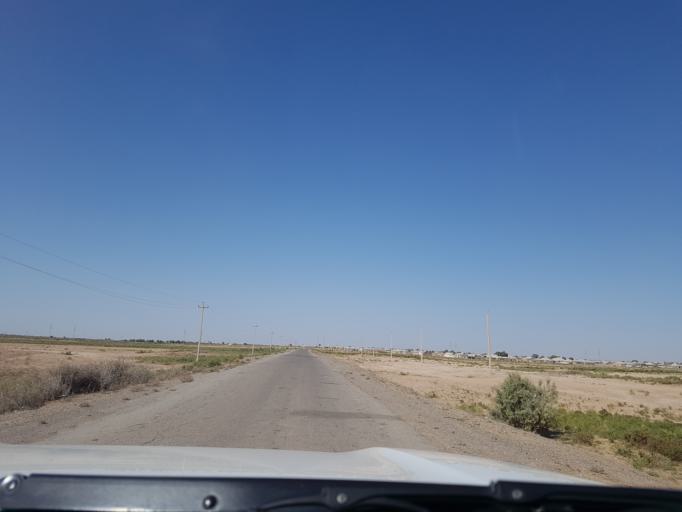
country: IR
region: Razavi Khorasan
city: Sarakhs
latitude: 36.5030
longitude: 61.2535
